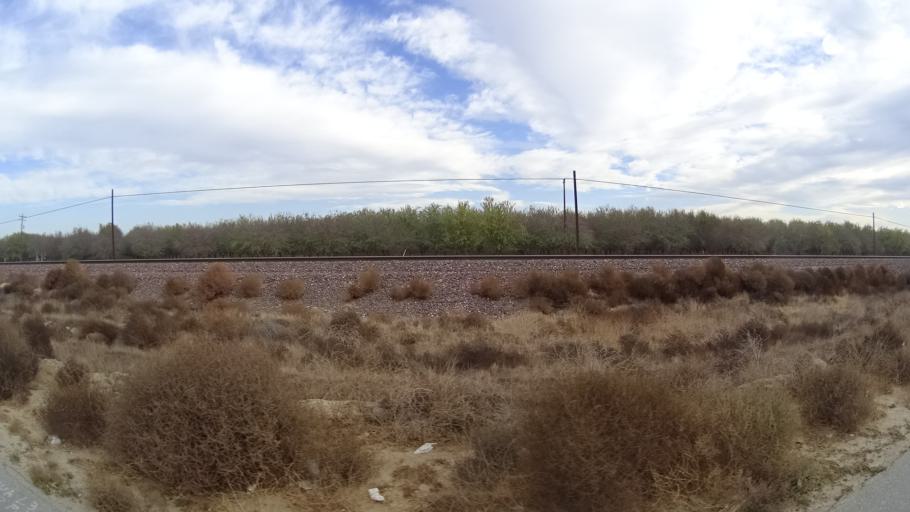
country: US
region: California
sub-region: Kern County
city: Rosedale
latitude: 35.4230
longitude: -119.1764
